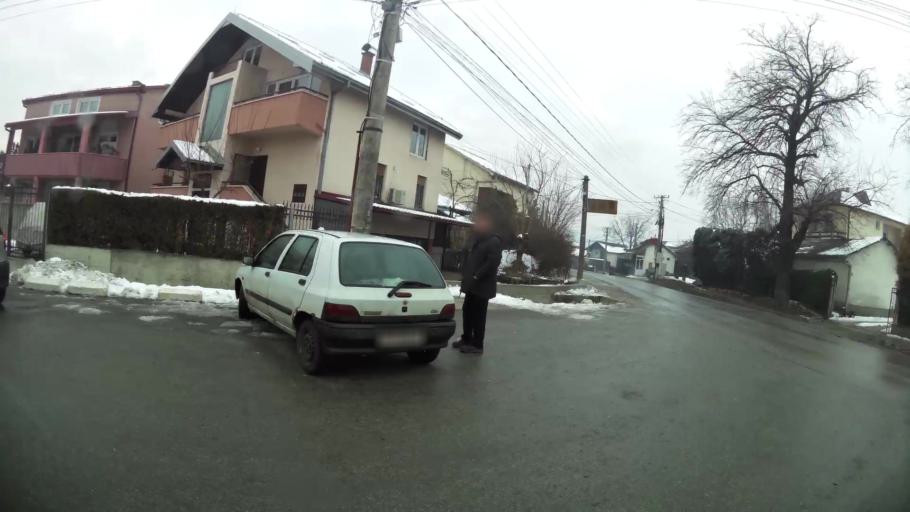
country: MK
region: Saraj
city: Saraj
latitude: 42.0283
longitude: 21.3538
